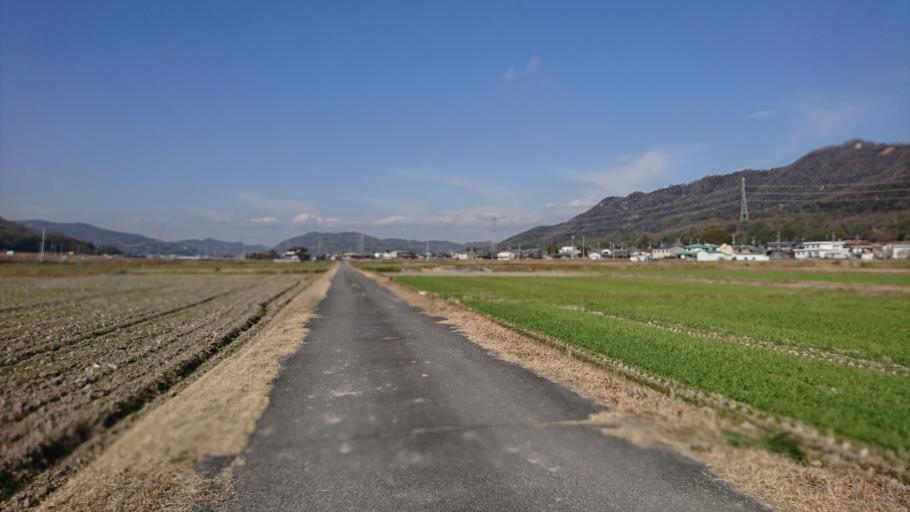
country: JP
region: Hyogo
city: Kakogawacho-honmachi
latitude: 34.8172
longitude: 134.8523
